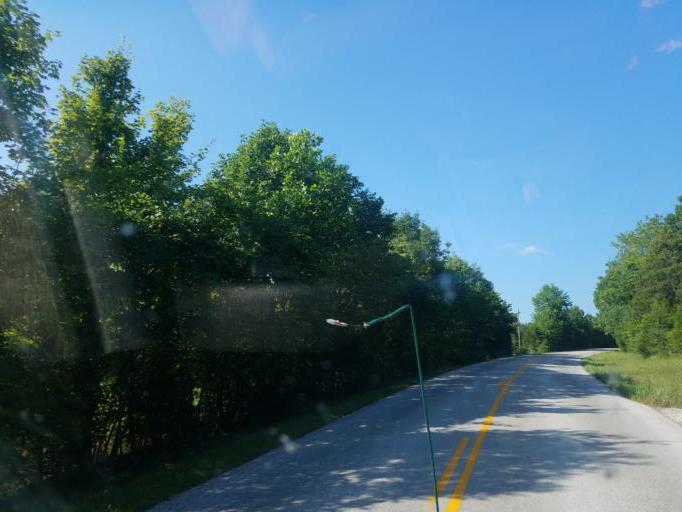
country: US
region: Kentucky
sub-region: Hart County
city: Munfordville
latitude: 37.3429
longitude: -86.0499
